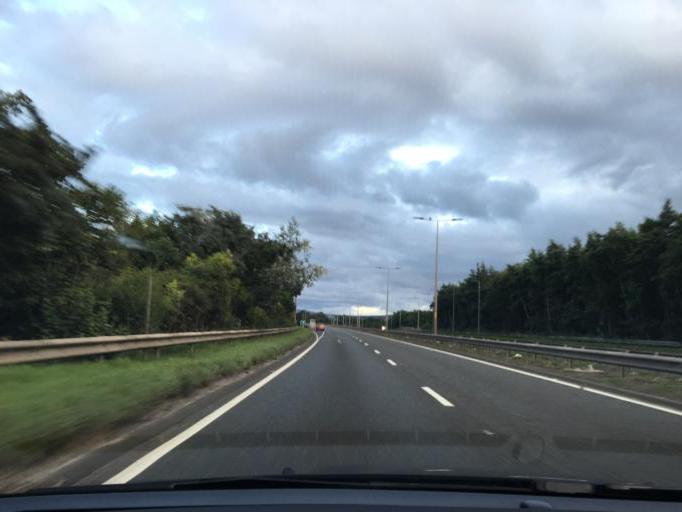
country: GB
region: Scotland
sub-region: Highland
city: Inverness
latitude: 57.4847
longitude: -4.2007
